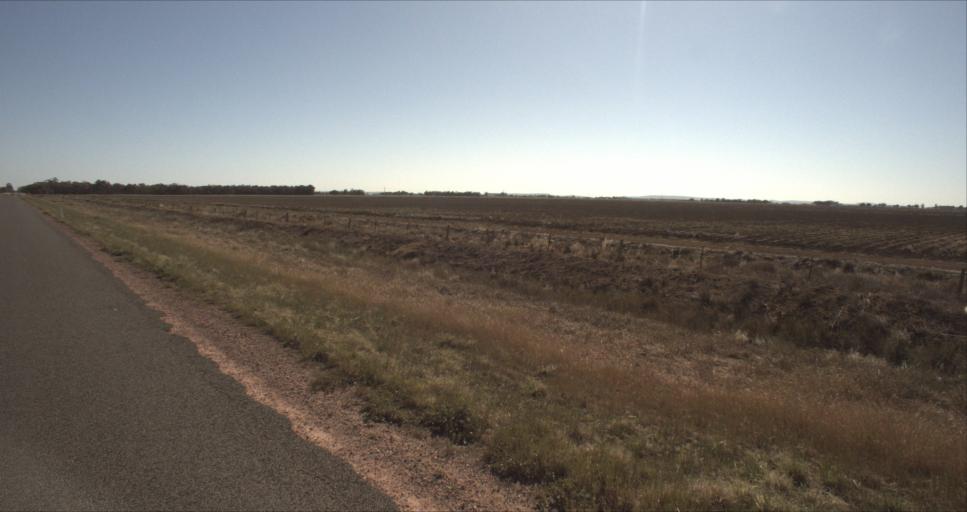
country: AU
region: New South Wales
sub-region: Leeton
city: Leeton
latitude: -34.5708
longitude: 146.2635
